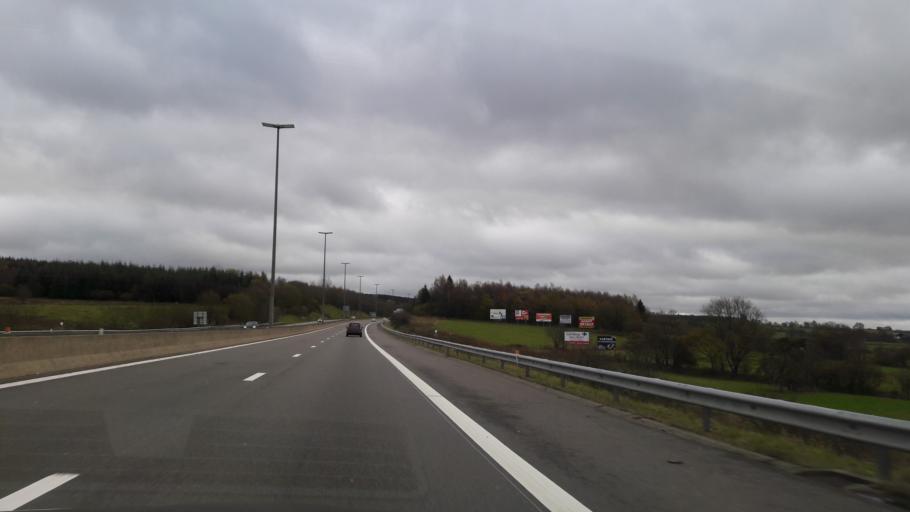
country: BE
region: Wallonia
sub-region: Province de Liege
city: Malmedy
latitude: 50.4728
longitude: 5.9790
